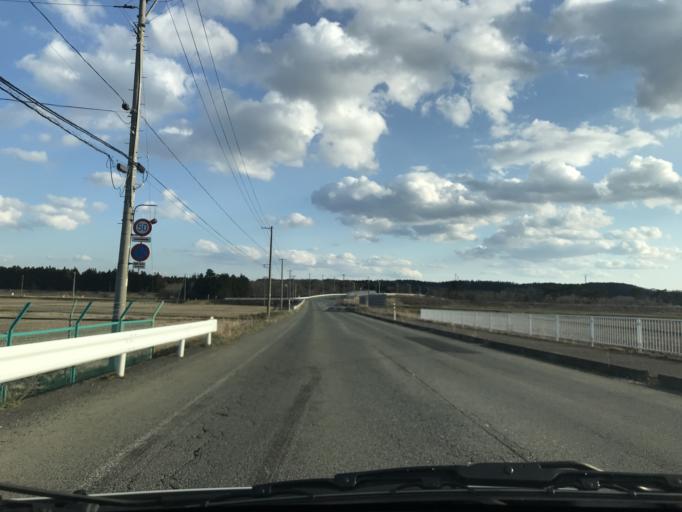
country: JP
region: Iwate
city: Kitakami
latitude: 39.2947
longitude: 141.0328
